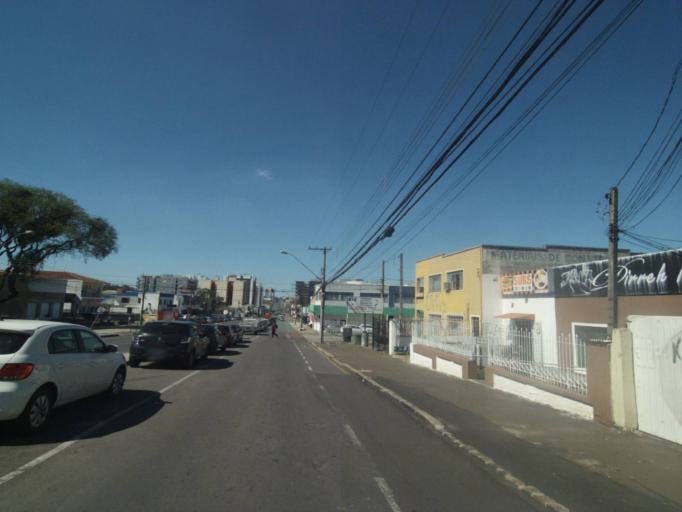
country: BR
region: Parana
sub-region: Curitiba
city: Curitiba
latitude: -25.3933
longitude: -49.2402
